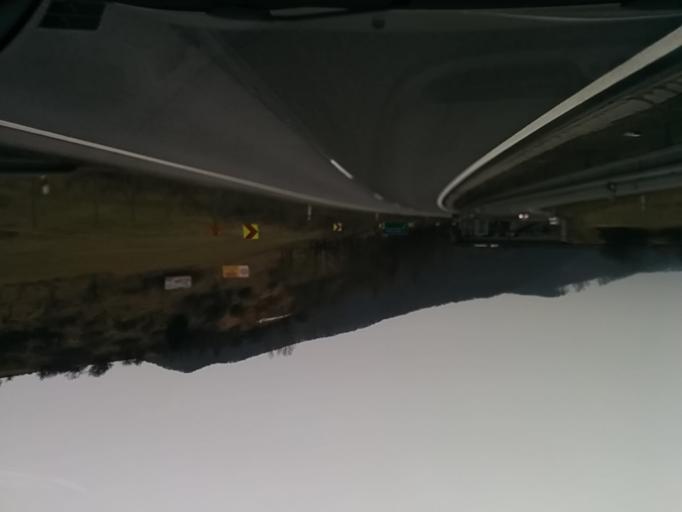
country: SK
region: Banskobystricky
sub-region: Okres Banska Bystrica
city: Zvolen
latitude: 48.5652
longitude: 19.0063
